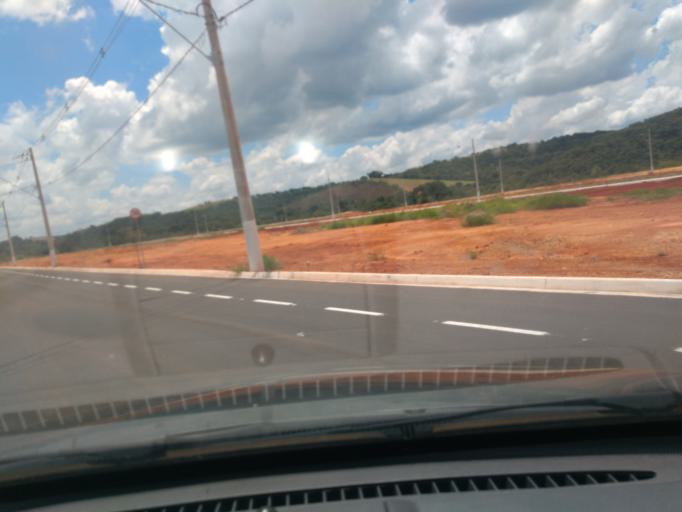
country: BR
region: Minas Gerais
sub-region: Tres Coracoes
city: Tres Coracoes
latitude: -21.6623
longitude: -45.2754
